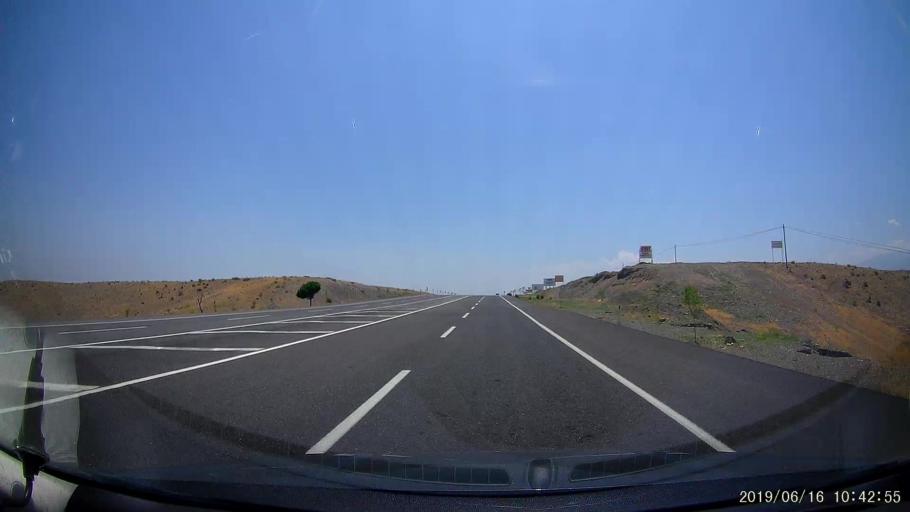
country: AM
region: Armavir
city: Shenavan
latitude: 40.0384
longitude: 43.8166
